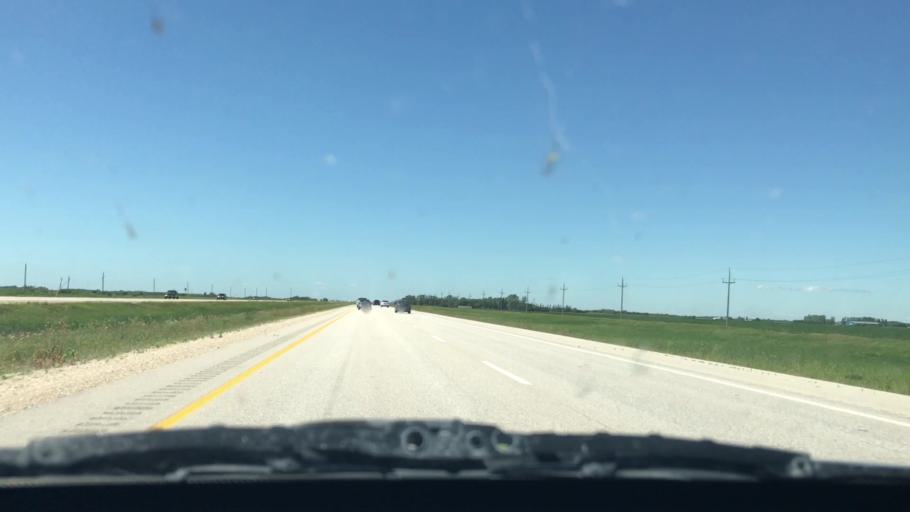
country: CA
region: Manitoba
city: Steinbach
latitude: 49.7357
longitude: -96.7325
